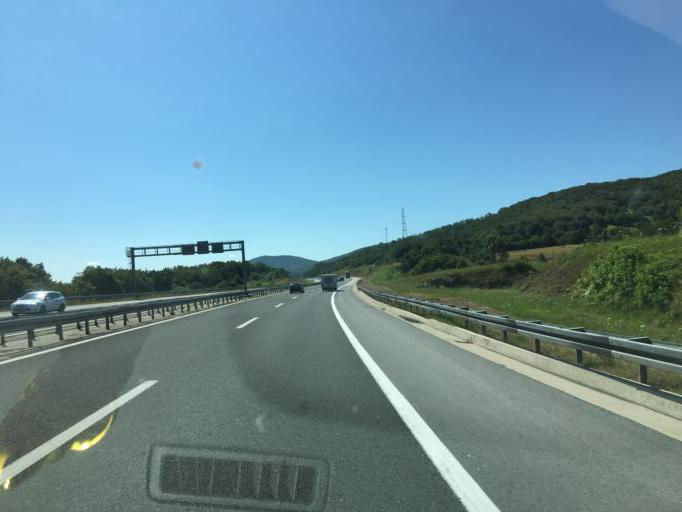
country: HR
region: Licko-Senjska
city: Brinje
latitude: 44.9461
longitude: 15.1611
